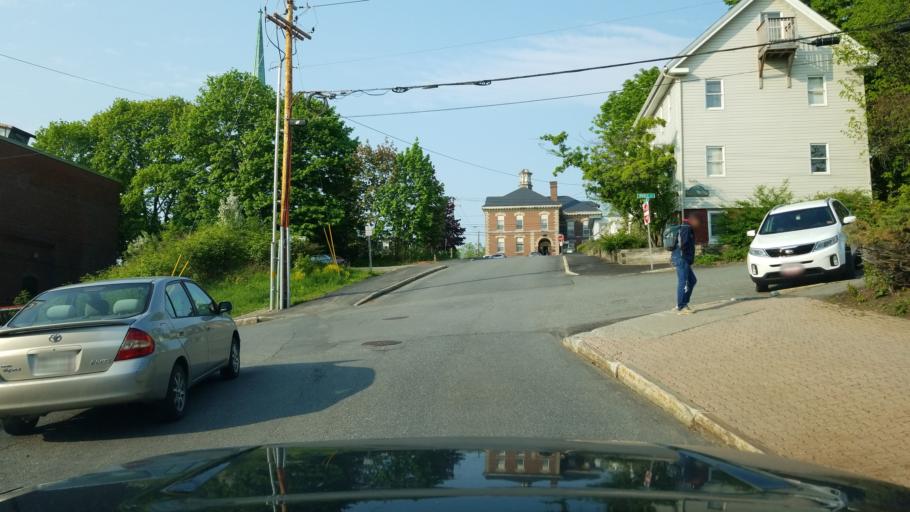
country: US
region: Maine
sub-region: Penobscot County
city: Bangor
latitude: 44.8000
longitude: -68.7730
